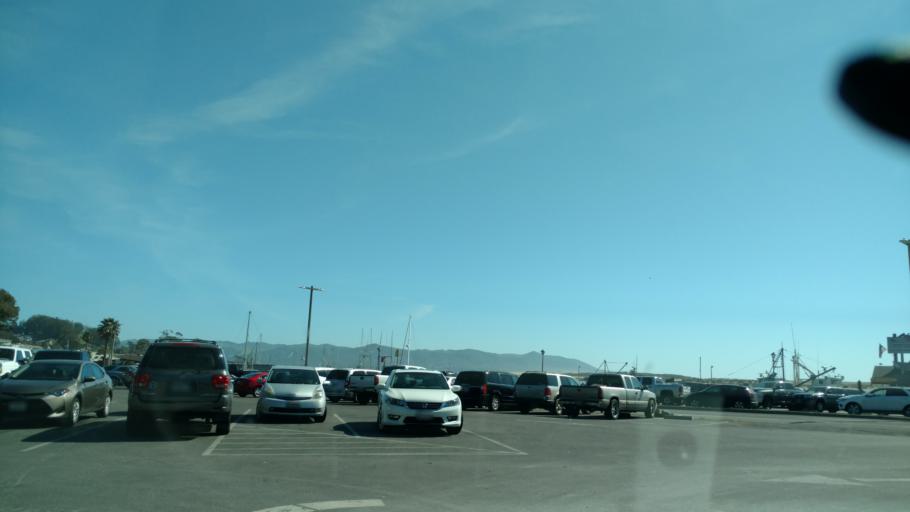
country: US
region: California
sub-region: San Luis Obispo County
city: Morro Bay
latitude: 35.3705
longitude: -120.8553
